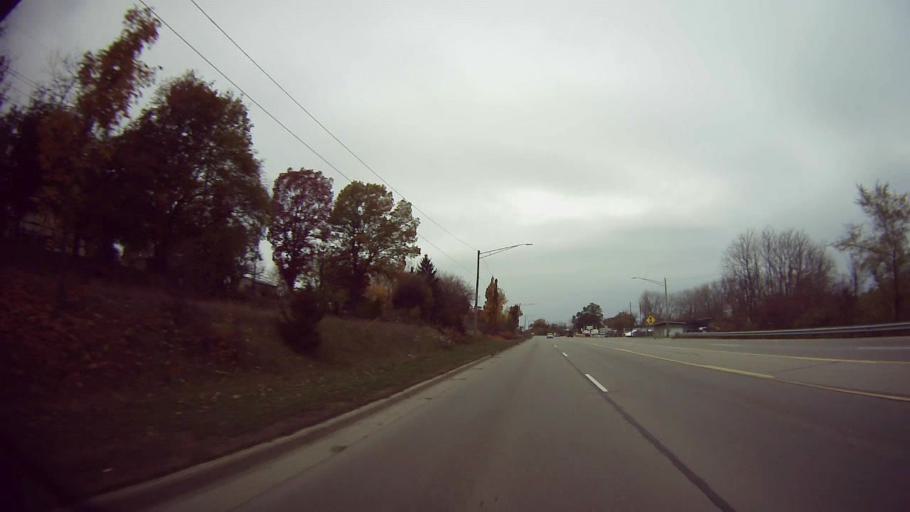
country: US
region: Michigan
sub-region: Oakland County
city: Waterford
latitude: 42.6787
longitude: -83.3664
